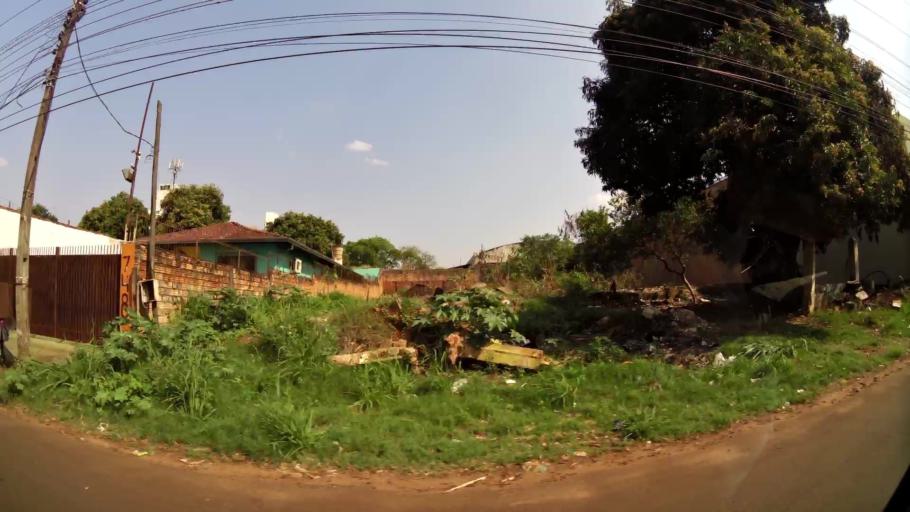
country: PY
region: Alto Parana
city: Ciudad del Este
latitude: -25.5096
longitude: -54.6244
